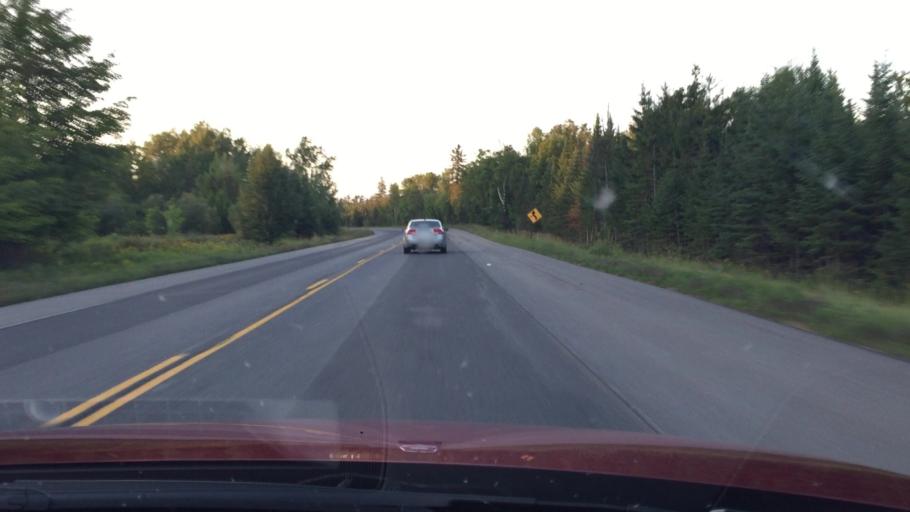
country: US
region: Maine
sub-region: Aroostook County
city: Houlton
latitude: 46.2851
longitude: -67.8396
